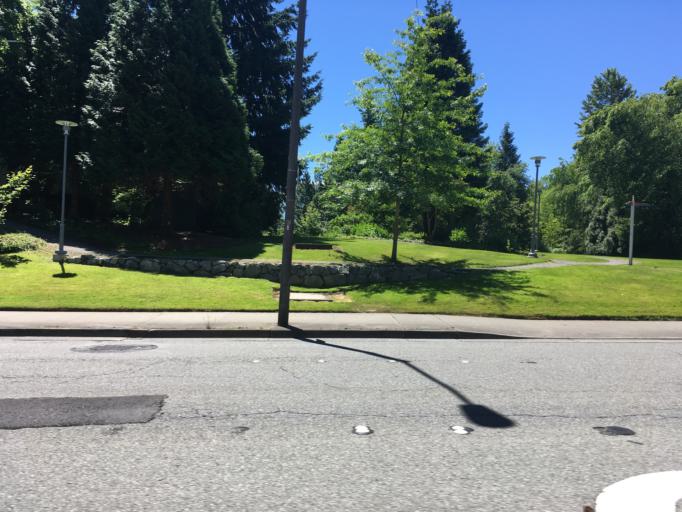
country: US
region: Washington
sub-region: King County
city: Redmond
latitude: 47.6460
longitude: -122.1307
